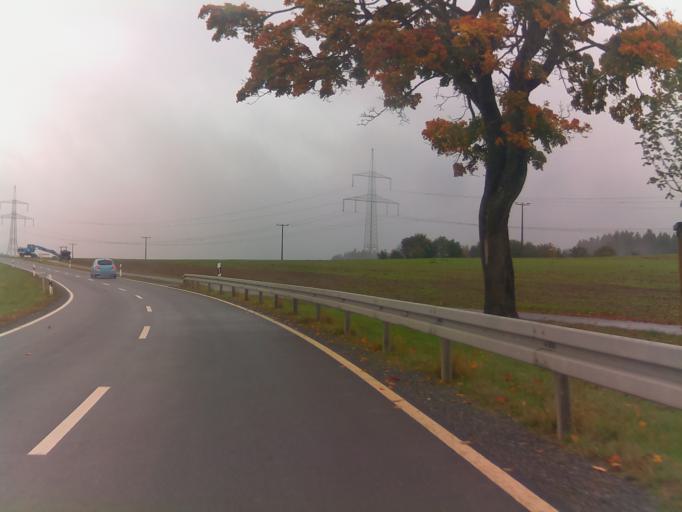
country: DE
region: Bavaria
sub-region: Upper Franconia
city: Wilhelmsthal
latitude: 50.3498
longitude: 11.4081
